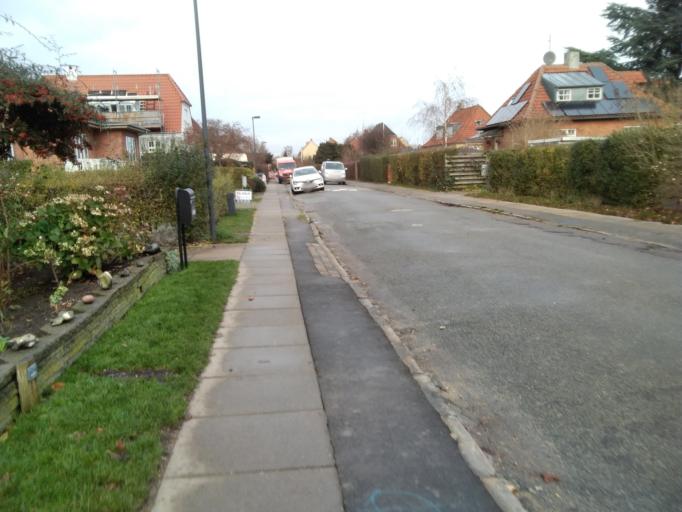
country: DK
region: Capital Region
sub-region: Tarnby Kommune
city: Tarnby
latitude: 55.6426
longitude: 12.6204
